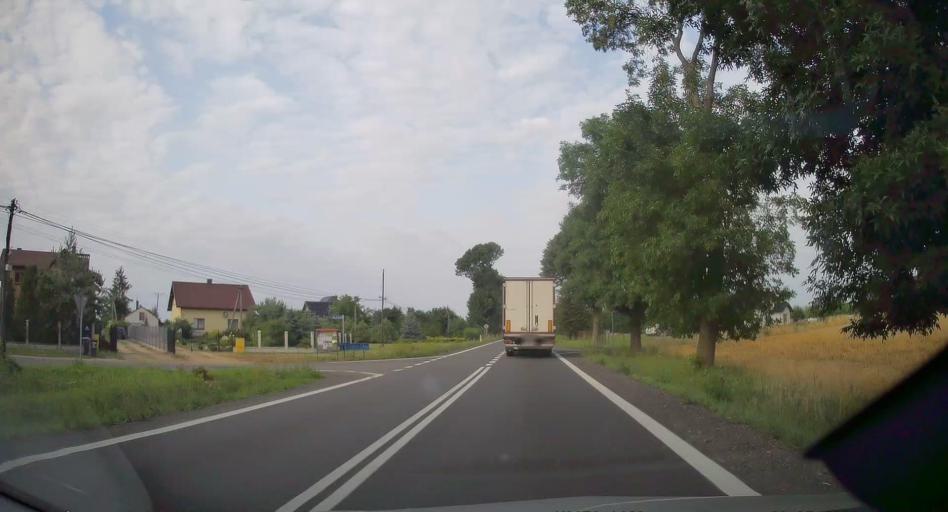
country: PL
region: Silesian Voivodeship
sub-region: Powiat czestochowski
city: Borowno
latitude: 50.9024
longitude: 19.2897
